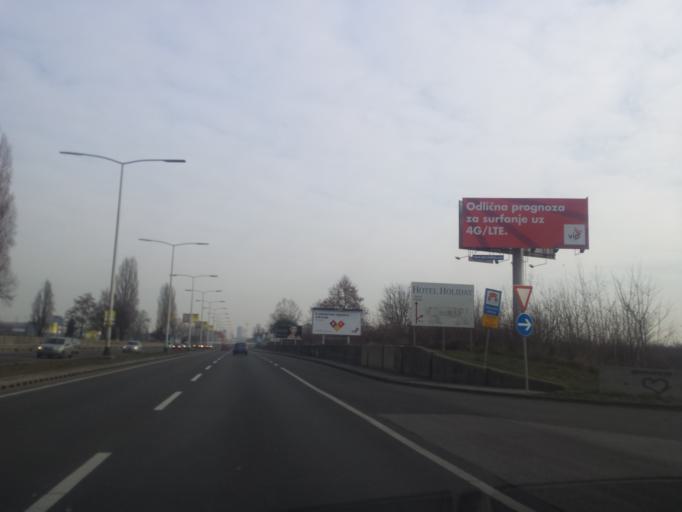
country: HR
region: Grad Zagreb
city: Stenjevec
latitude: 45.7974
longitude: 15.8766
